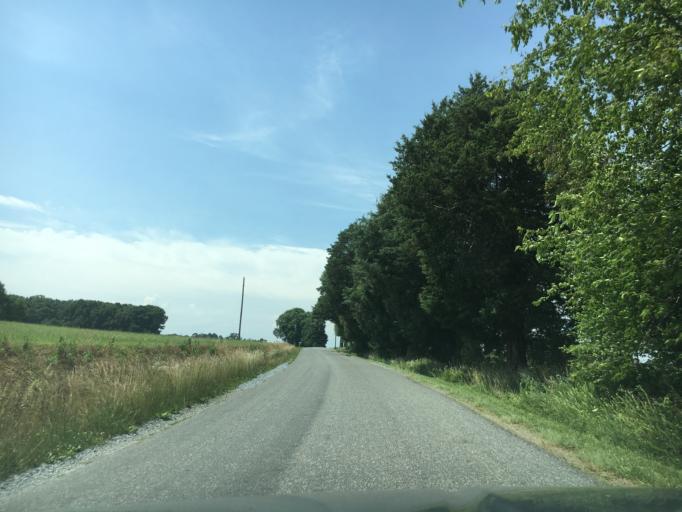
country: US
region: Virginia
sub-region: Pittsylvania County
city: Gretna
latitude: 36.9165
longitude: -79.4218
